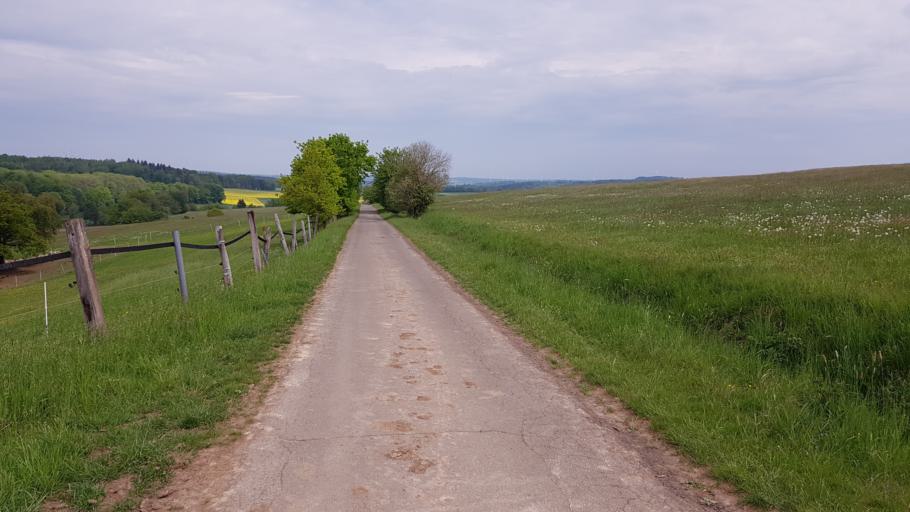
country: DE
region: Hesse
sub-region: Regierungsbezirk Giessen
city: Grunberg
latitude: 50.6396
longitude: 9.0105
